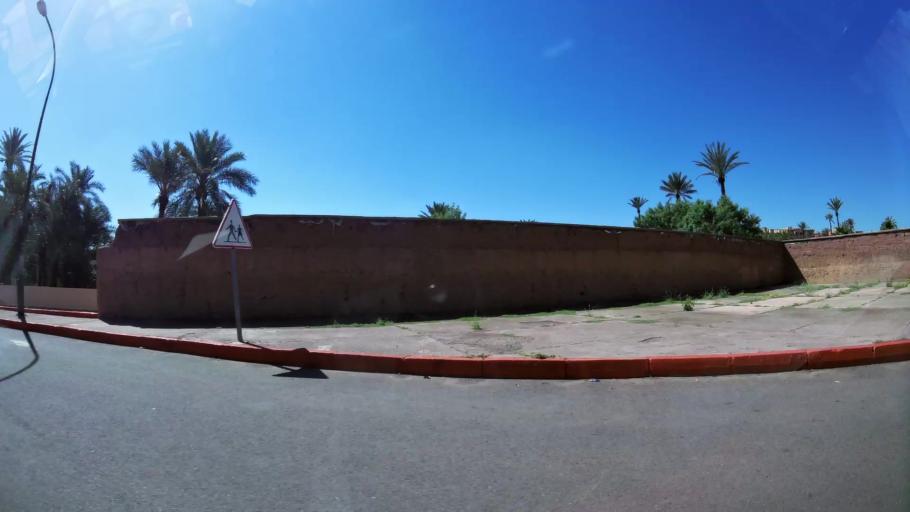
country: MA
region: Marrakech-Tensift-Al Haouz
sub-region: Marrakech
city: Marrakesh
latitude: 31.6411
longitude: -8.0088
